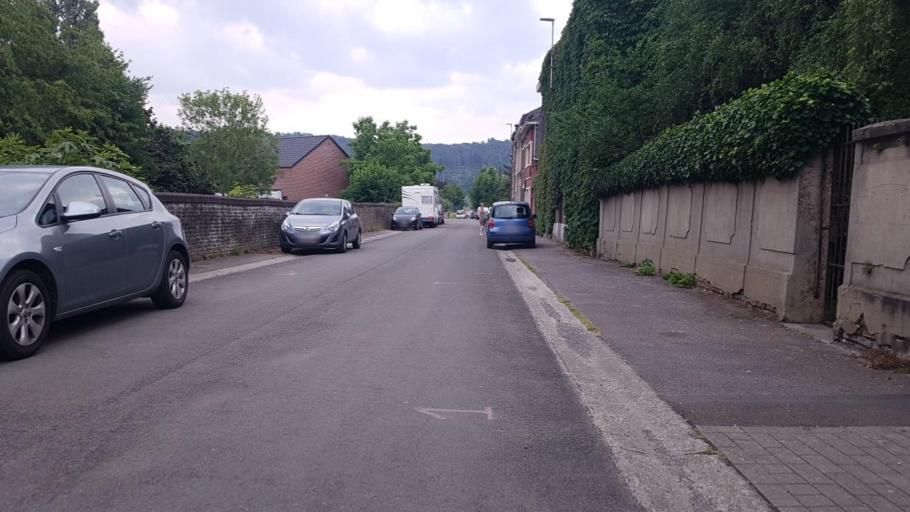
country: BE
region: Wallonia
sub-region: Province de Liege
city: Amay
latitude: 50.5459
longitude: 5.3218
